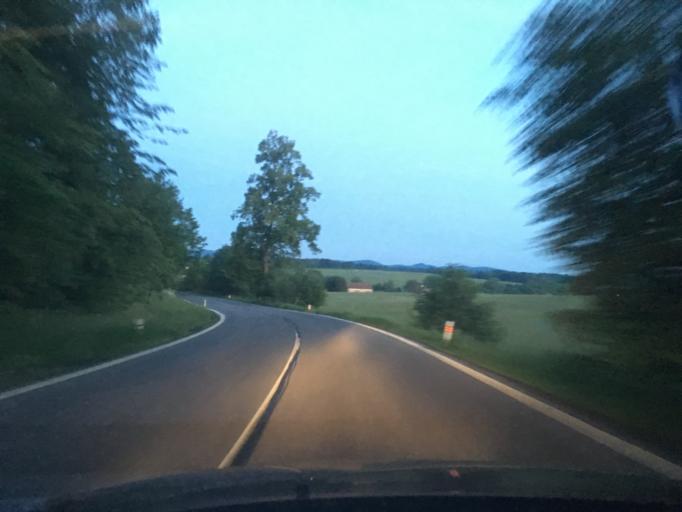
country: PL
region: Silesian Voivodeship
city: Zawidow
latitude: 50.9841
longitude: 15.0747
